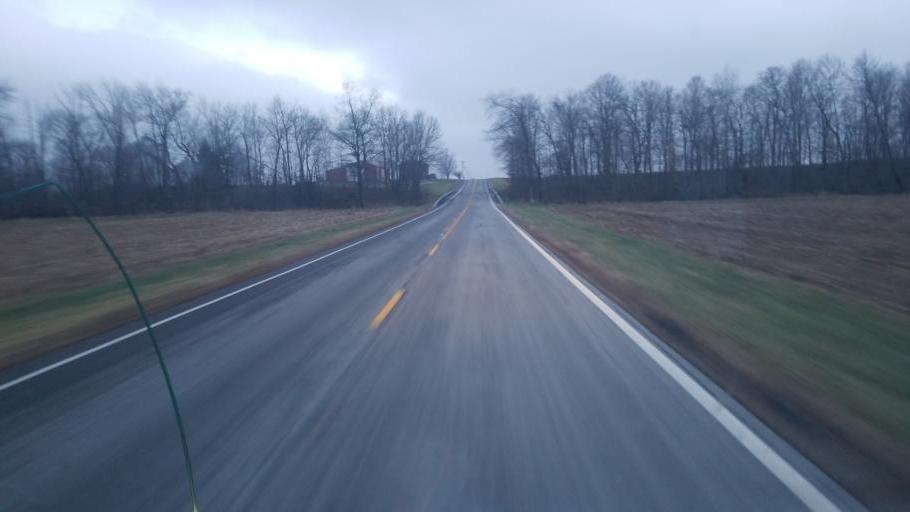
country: US
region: Ohio
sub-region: Wyandot County
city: Upper Sandusky
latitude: 40.8490
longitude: -83.1315
